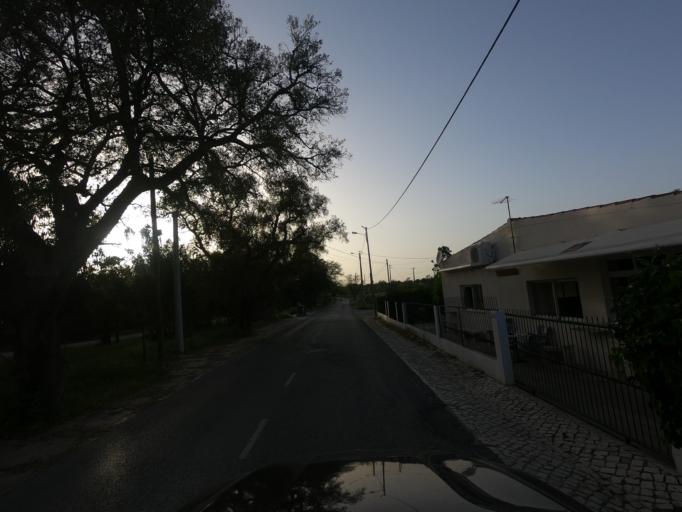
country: PT
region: Setubal
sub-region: Setubal
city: Setubal
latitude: 38.5325
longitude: -8.8142
